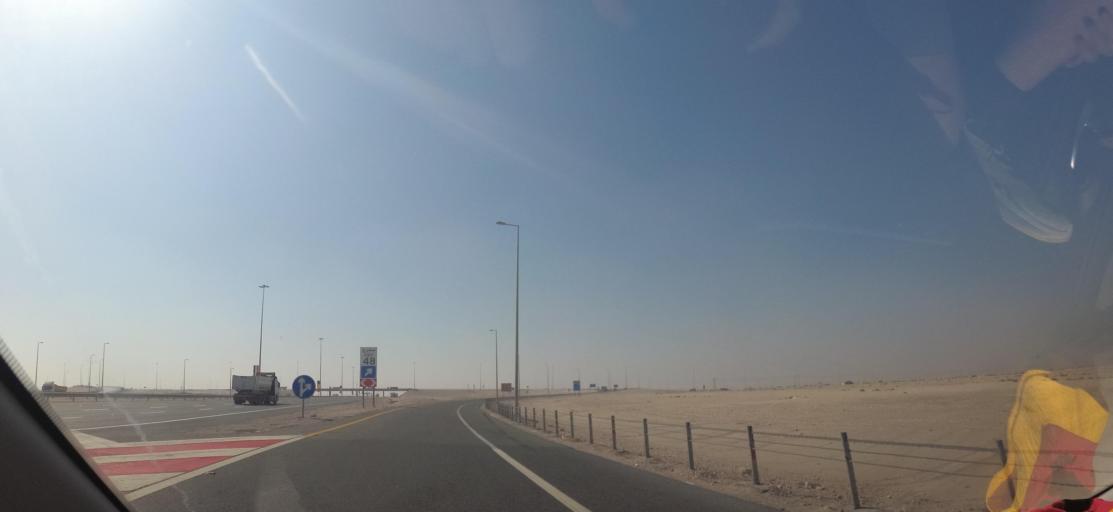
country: QA
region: Baladiyat ar Rayyan
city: Ash Shahaniyah
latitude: 25.1119
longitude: 51.1722
